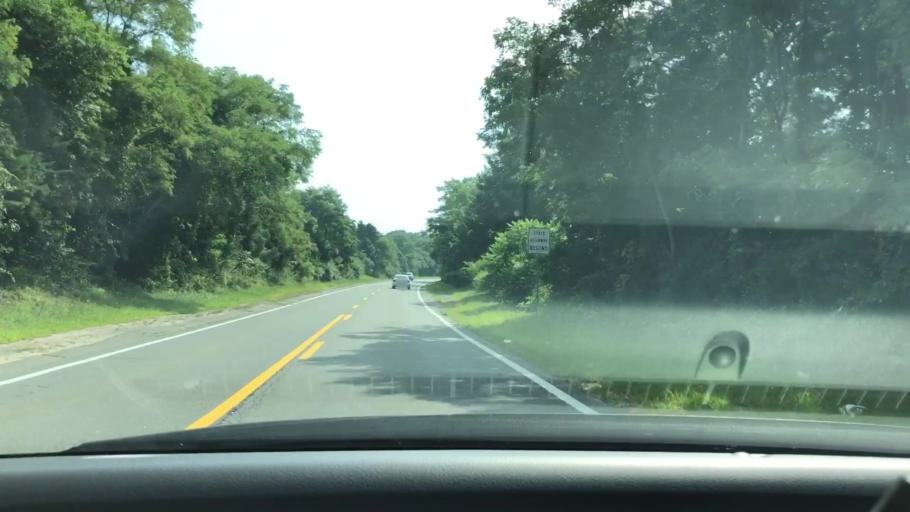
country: US
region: Massachusetts
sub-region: Barnstable County
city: Sagamore
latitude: 41.7803
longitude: -70.5349
